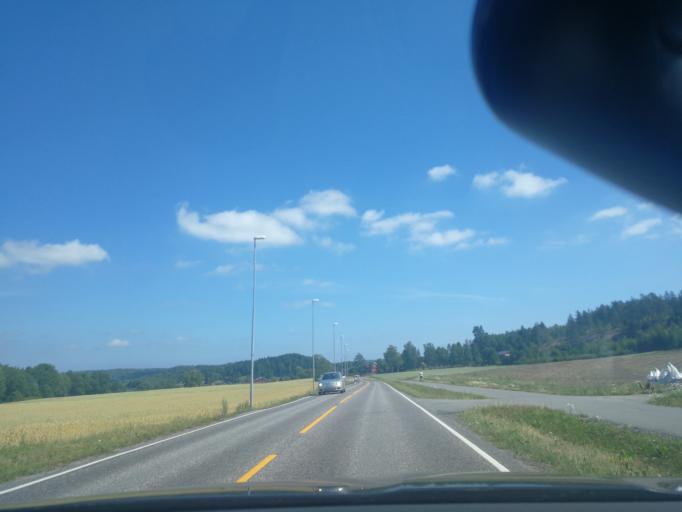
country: NO
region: Vestfold
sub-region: Stokke
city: Stokke
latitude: 59.2266
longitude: 10.3135
